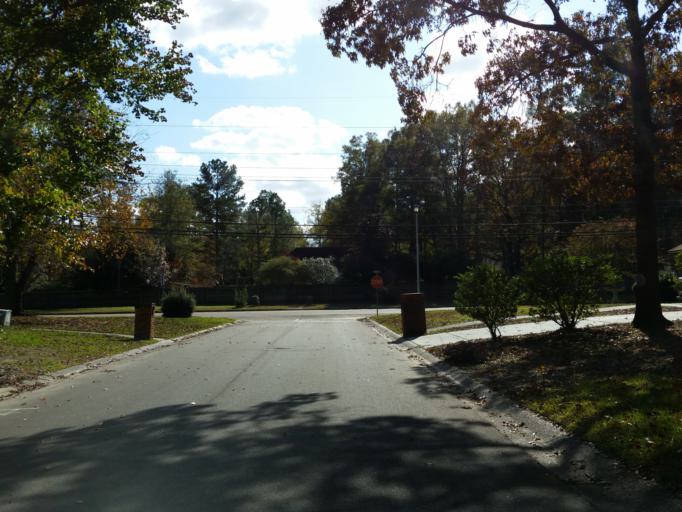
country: US
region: Mississippi
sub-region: Lamar County
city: West Hattiesburg
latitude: 31.3047
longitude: -89.3390
